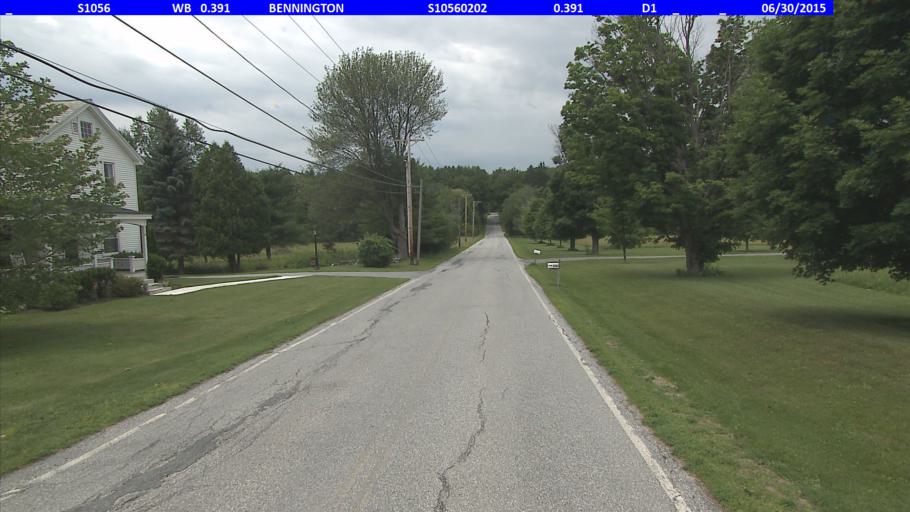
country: US
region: Vermont
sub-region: Bennington County
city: Bennington
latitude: 42.8877
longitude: -73.2218
